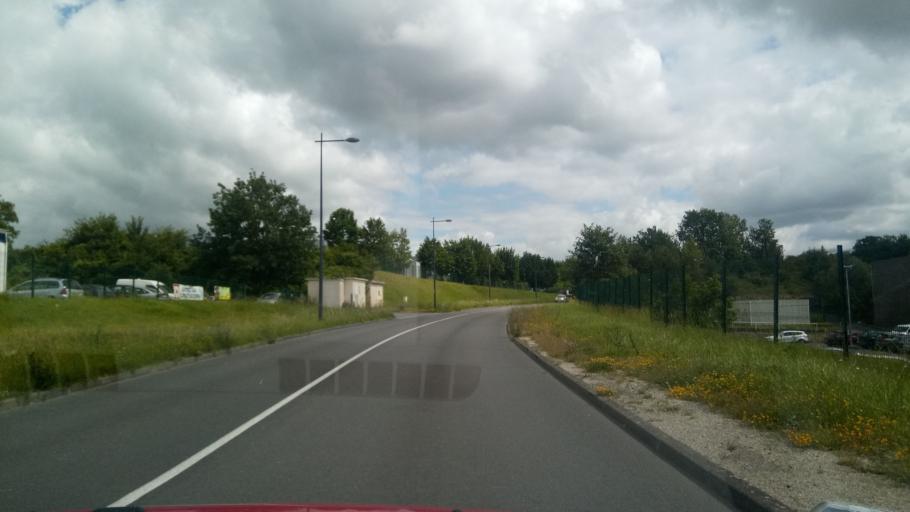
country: FR
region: Poitou-Charentes
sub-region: Departement de la Charente
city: Linars
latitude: 45.6315
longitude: 0.0733
